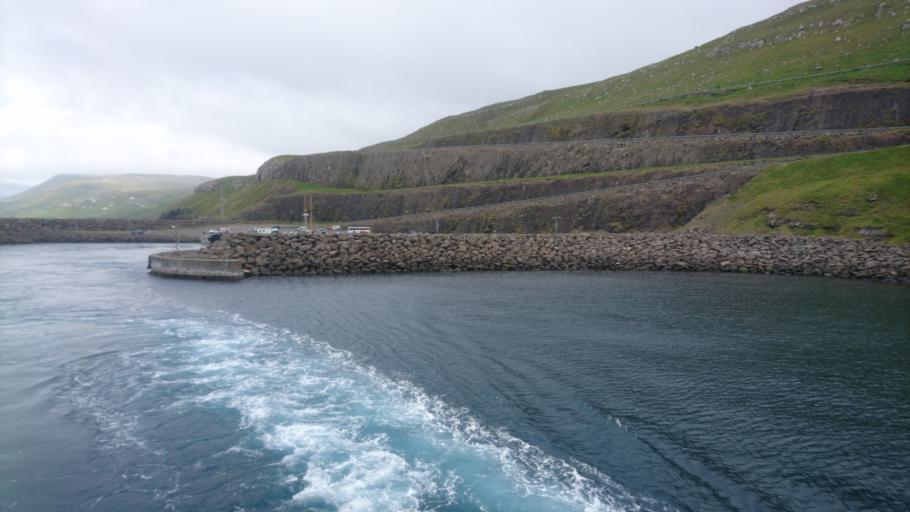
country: FO
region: Streymoy
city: Argir
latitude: 61.9602
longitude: -6.8164
